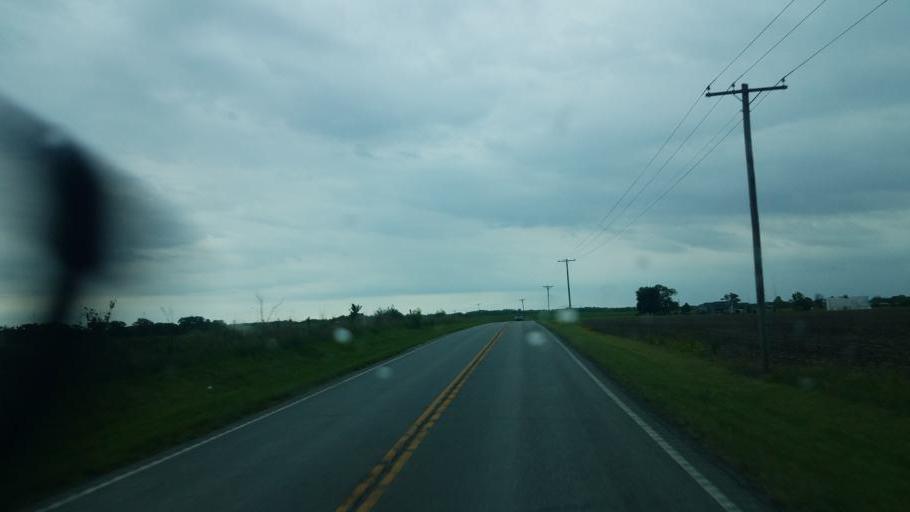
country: US
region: Missouri
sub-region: Cooper County
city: Boonville
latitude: 38.8535
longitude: -92.6355
